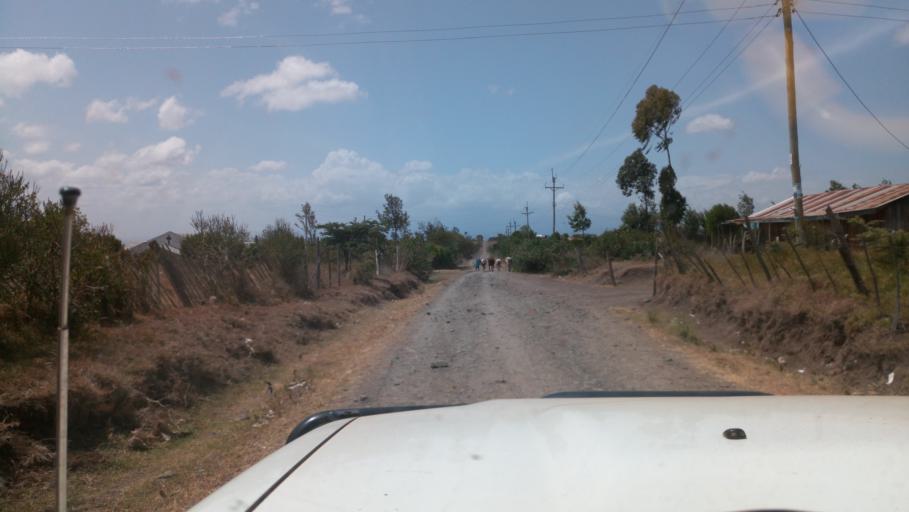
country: KE
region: Laikipia
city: Naro Moru
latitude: -0.1670
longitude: 36.8210
